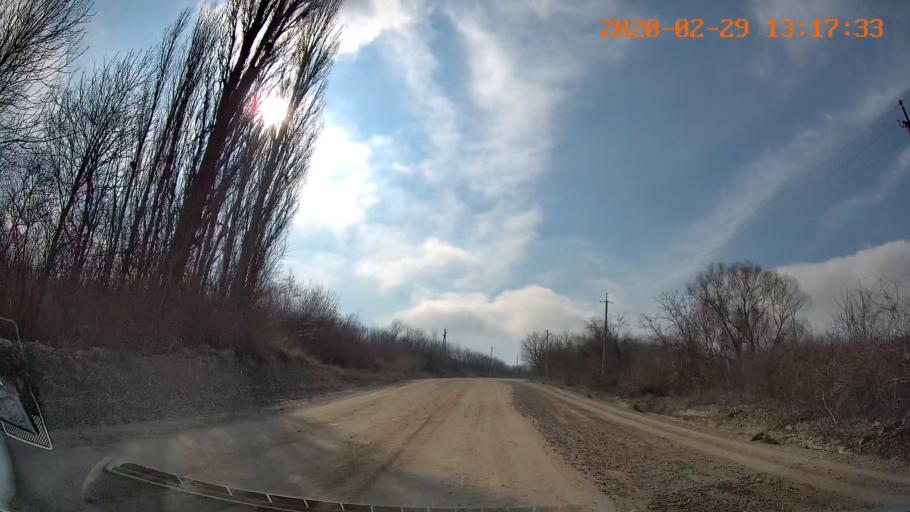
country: MD
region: Telenesti
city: Camenca
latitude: 47.9960
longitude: 28.6625
